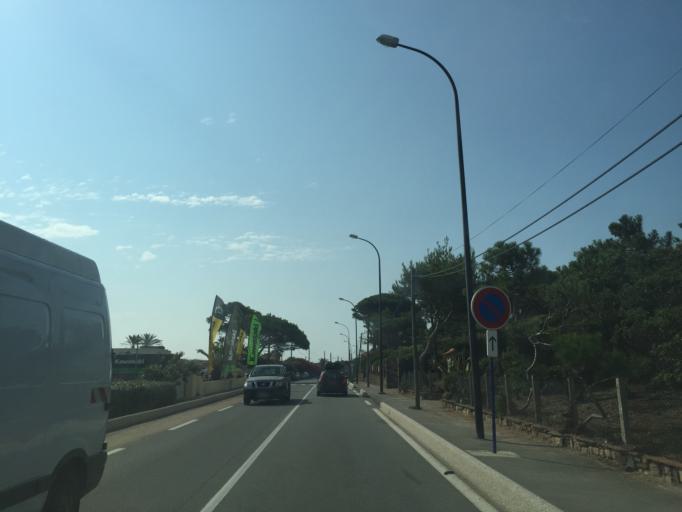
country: FR
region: Provence-Alpes-Cote d'Azur
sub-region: Departement du Var
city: Sainte-Maxime
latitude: 43.3172
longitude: 6.6664
